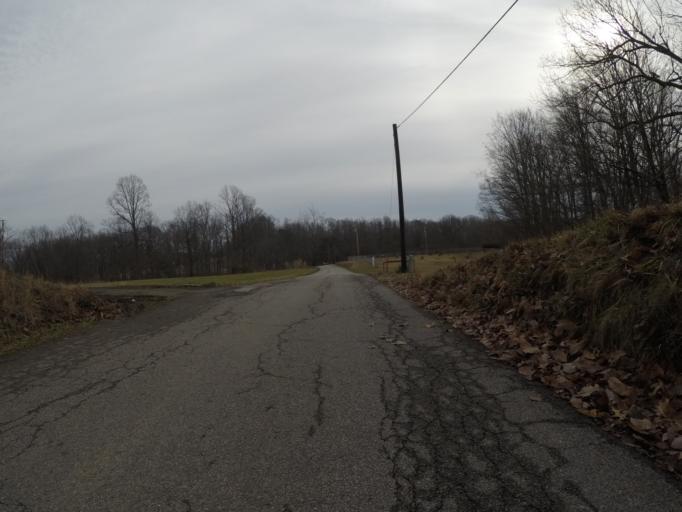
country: US
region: West Virginia
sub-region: Wayne County
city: Lavalette
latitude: 38.3549
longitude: -82.4106
